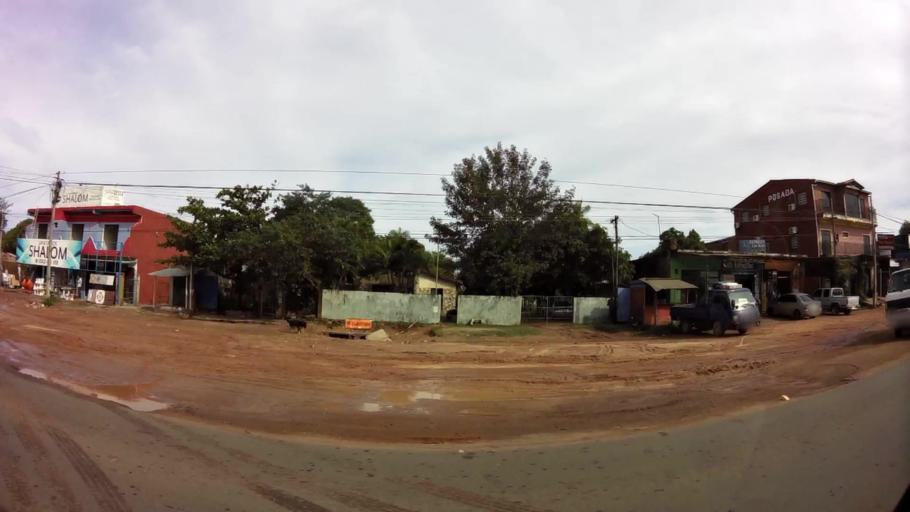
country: PY
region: Central
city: Limpio
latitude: -25.1739
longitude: -57.4830
